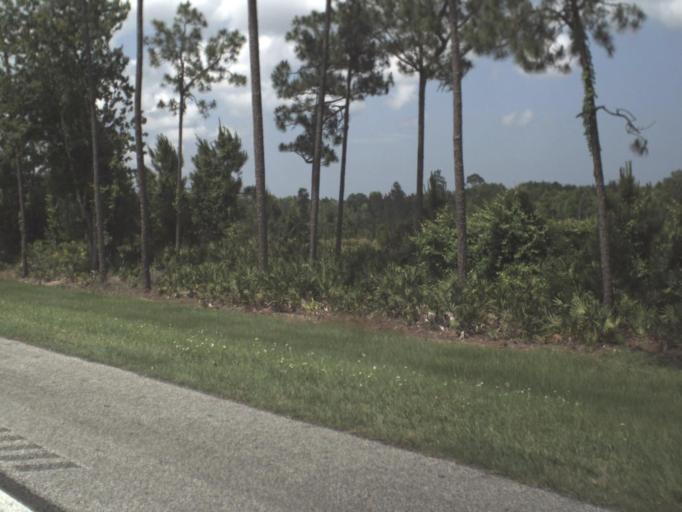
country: US
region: Florida
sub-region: Saint Johns County
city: Saint Augustine Shores
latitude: 29.7257
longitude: -81.3375
